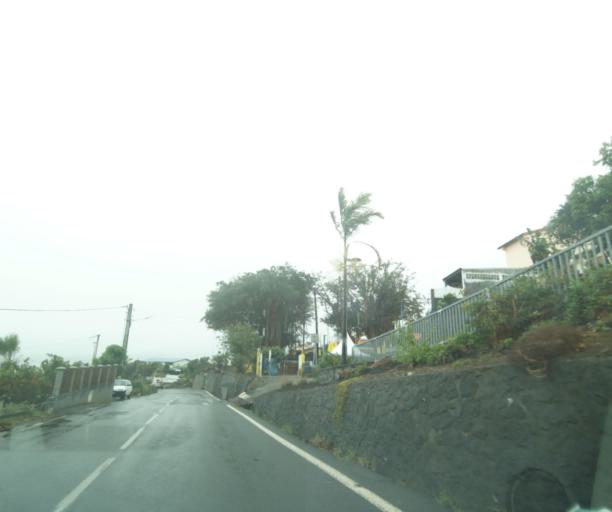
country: RE
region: Reunion
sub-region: Reunion
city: Saint-Paul
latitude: -21.0284
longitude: 55.2858
